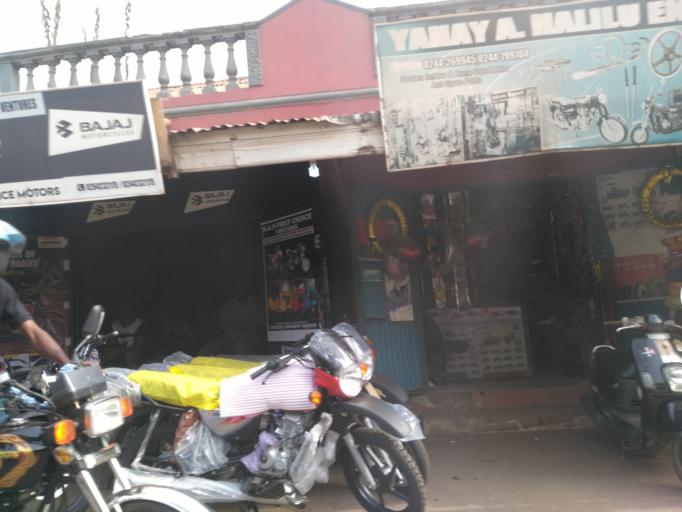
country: GH
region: Ashanti
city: Kumasi
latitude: 6.6988
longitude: -1.6162
